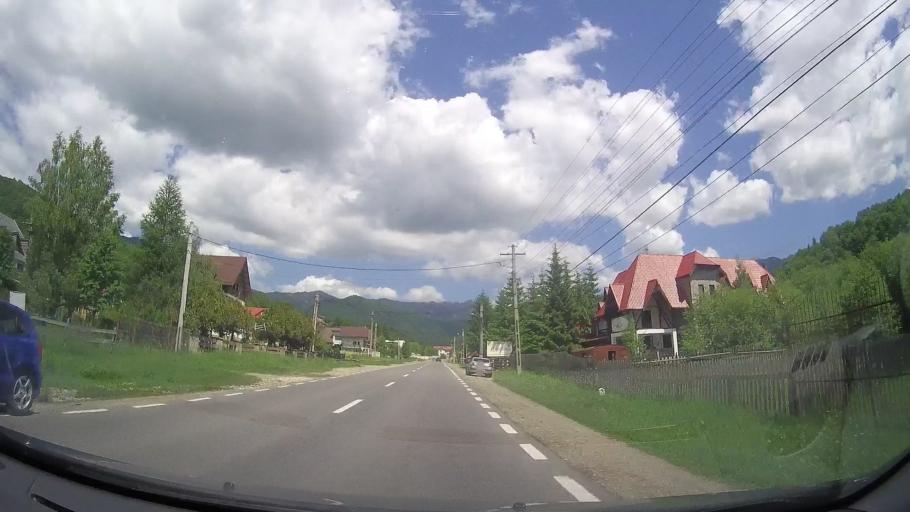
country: RO
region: Prahova
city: Maneciu
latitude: 45.4464
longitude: 25.9371
